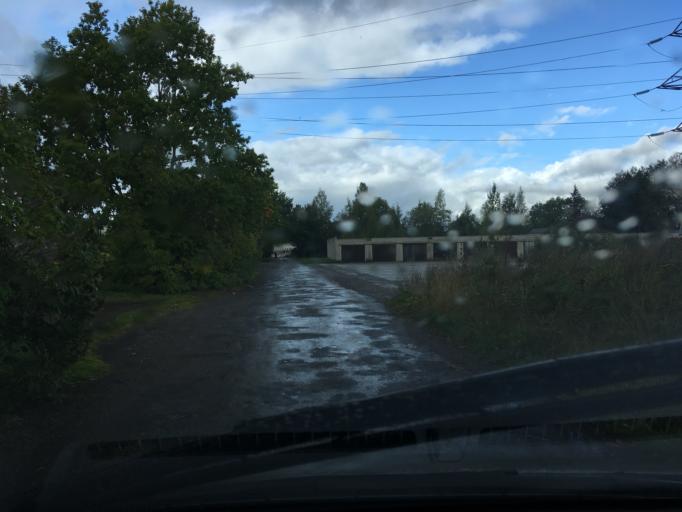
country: EE
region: Raplamaa
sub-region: Rapla vald
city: Rapla
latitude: 58.9947
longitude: 24.8136
